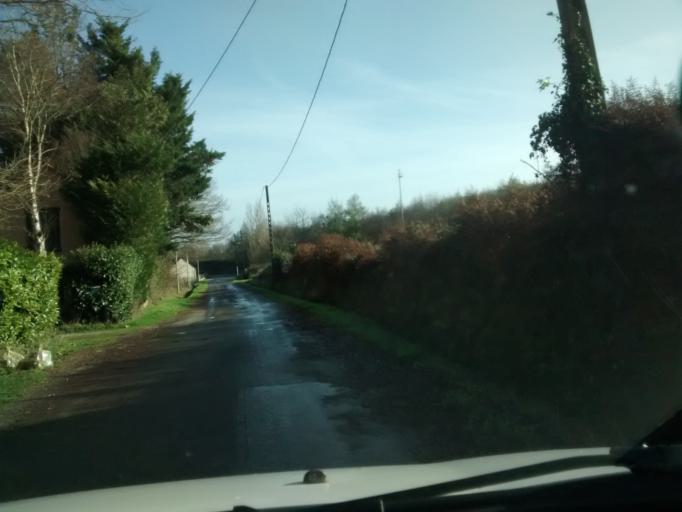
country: FR
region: Brittany
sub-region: Departement d'Ille-et-Vilaine
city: Cesson-Sevigne
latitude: 48.1455
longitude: -1.6219
